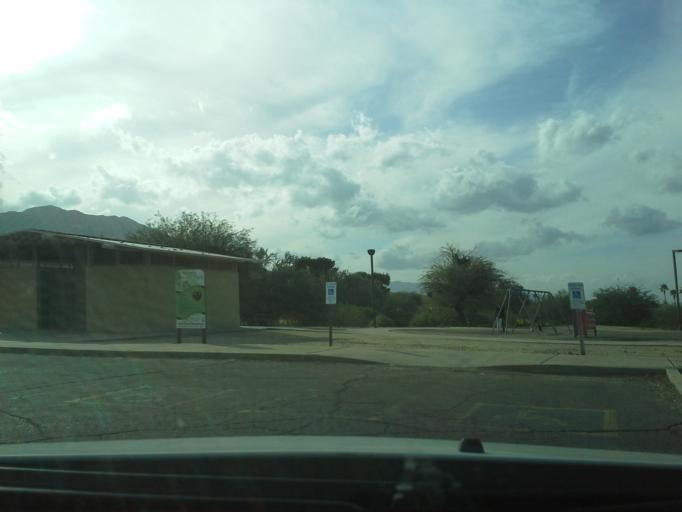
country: US
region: Arizona
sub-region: Maricopa County
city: Laveen
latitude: 33.3576
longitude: -112.0839
